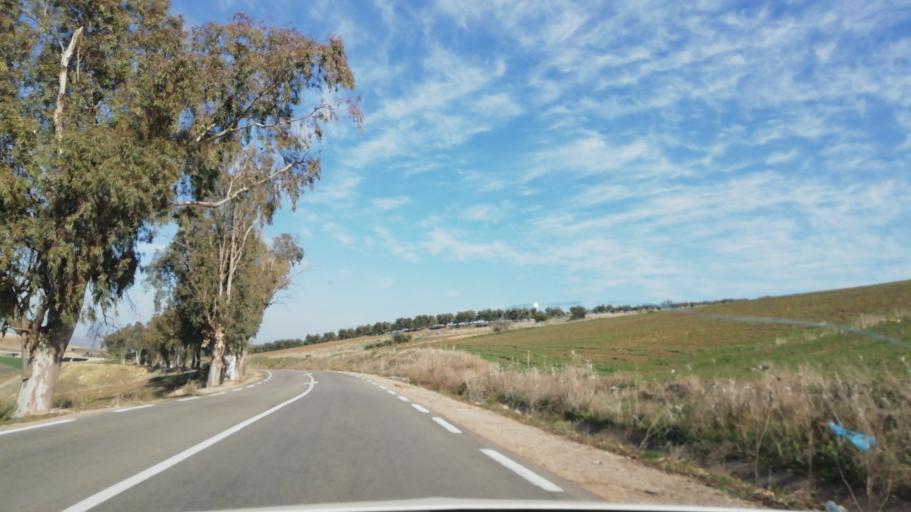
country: DZ
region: Tlemcen
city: Chetouane
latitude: 34.9667
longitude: -1.2467
